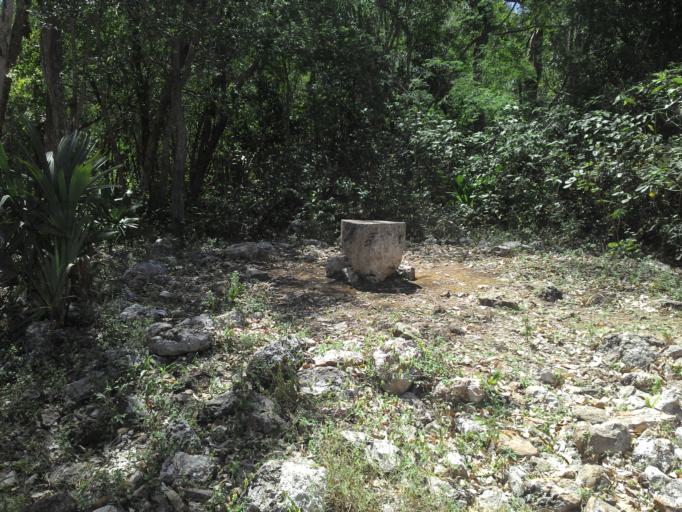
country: MX
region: Yucatan
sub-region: Oxkutzcab
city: Xul
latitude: 20.1710
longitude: -89.5784
